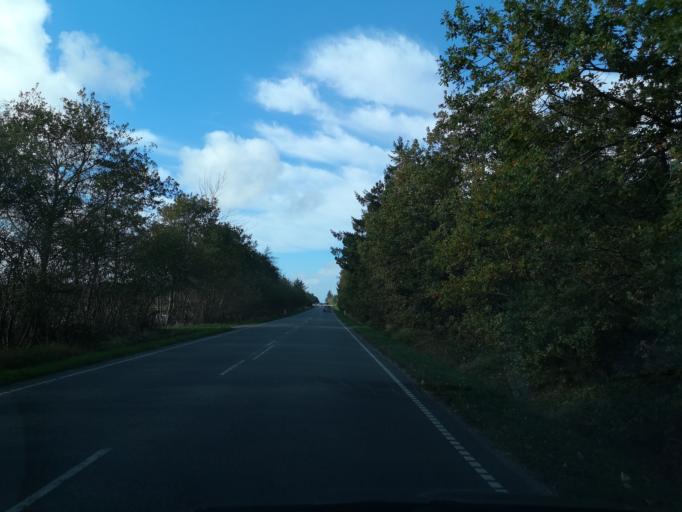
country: DK
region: South Denmark
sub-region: Varde Kommune
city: Oksbol
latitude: 55.7298
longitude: 8.2199
